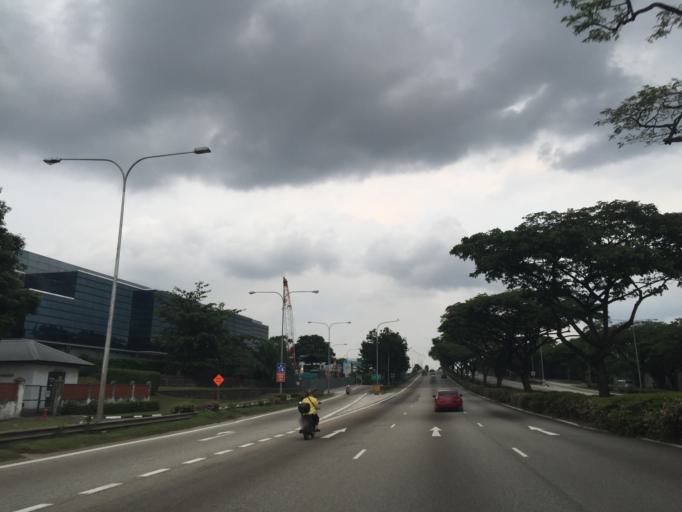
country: SG
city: Singapore
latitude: 1.3221
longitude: 103.7040
